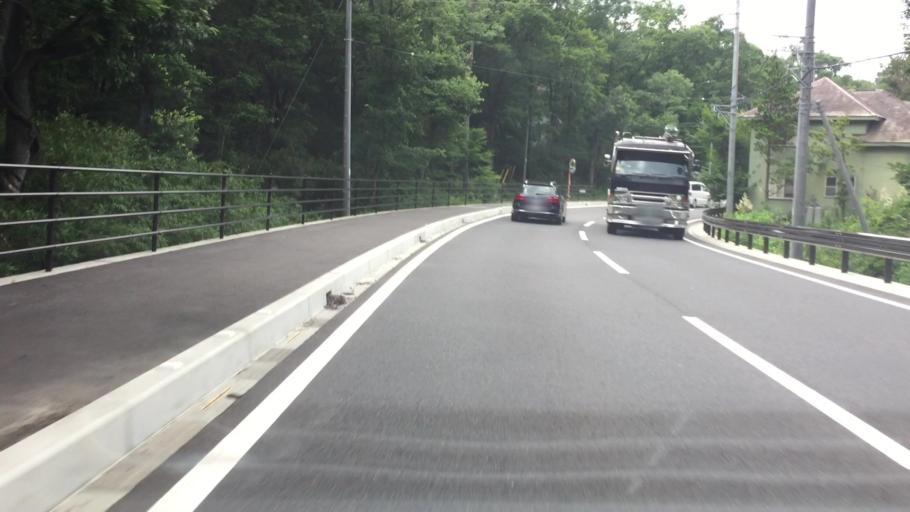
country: JP
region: Tochigi
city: Kuroiso
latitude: 37.0647
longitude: 140.0427
